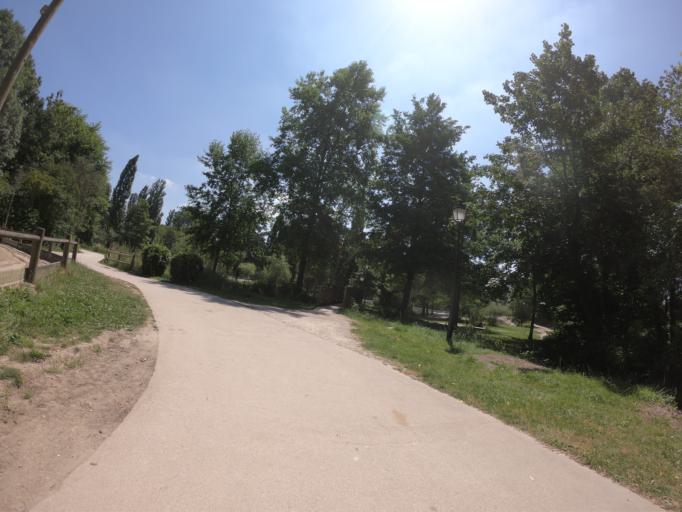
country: FR
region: Ile-de-France
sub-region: Departement des Hauts-de-Seine
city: Antony
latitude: 48.7459
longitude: 2.2874
